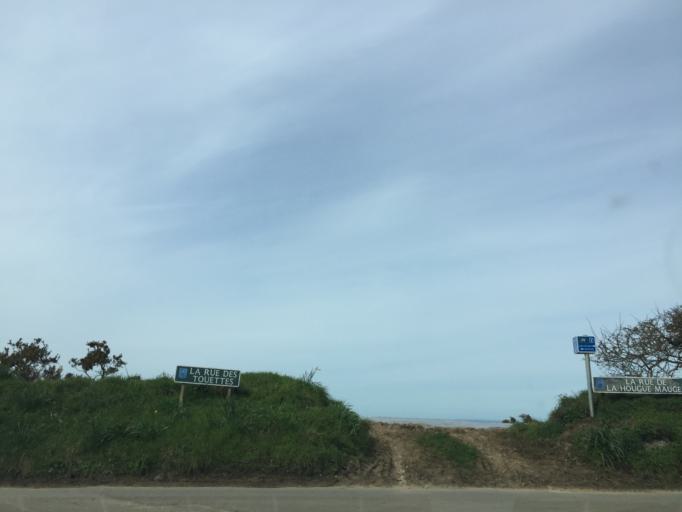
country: JE
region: St Helier
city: Saint Helier
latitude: 49.2445
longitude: -2.1743
